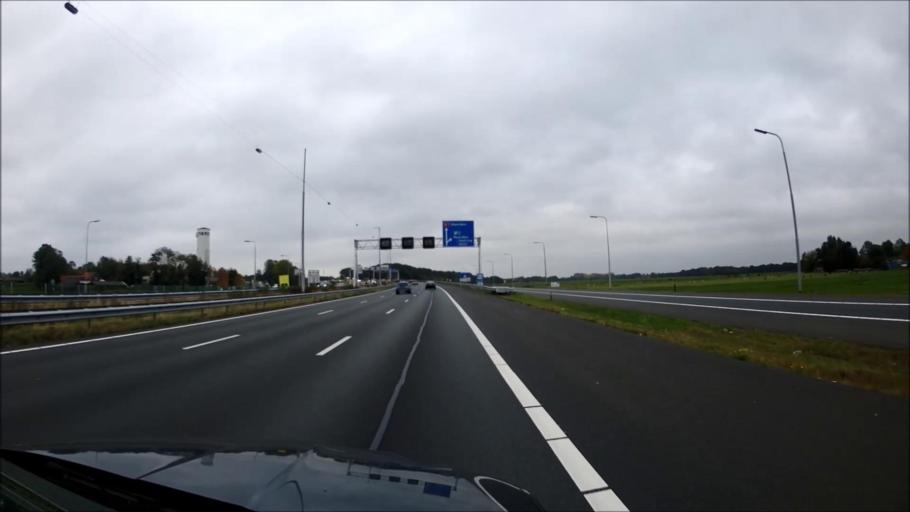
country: NL
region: North Holland
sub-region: Gemeente Naarden
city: Naarden
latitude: 52.3072
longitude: 5.1280
